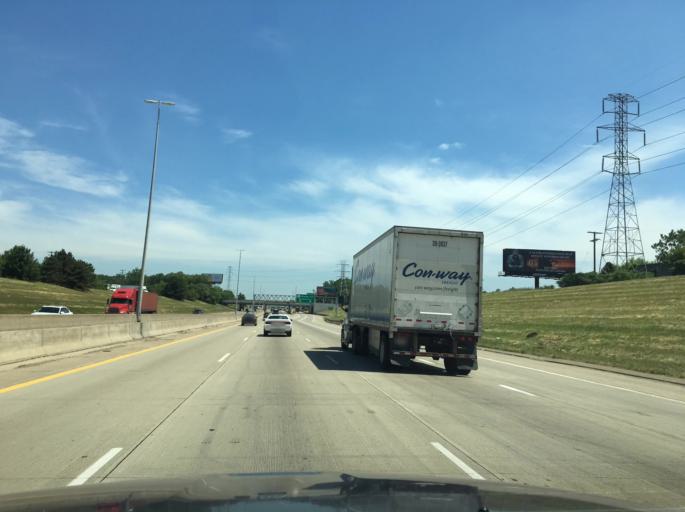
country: US
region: Michigan
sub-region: Wayne County
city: Dearborn
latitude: 42.3177
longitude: -83.1675
